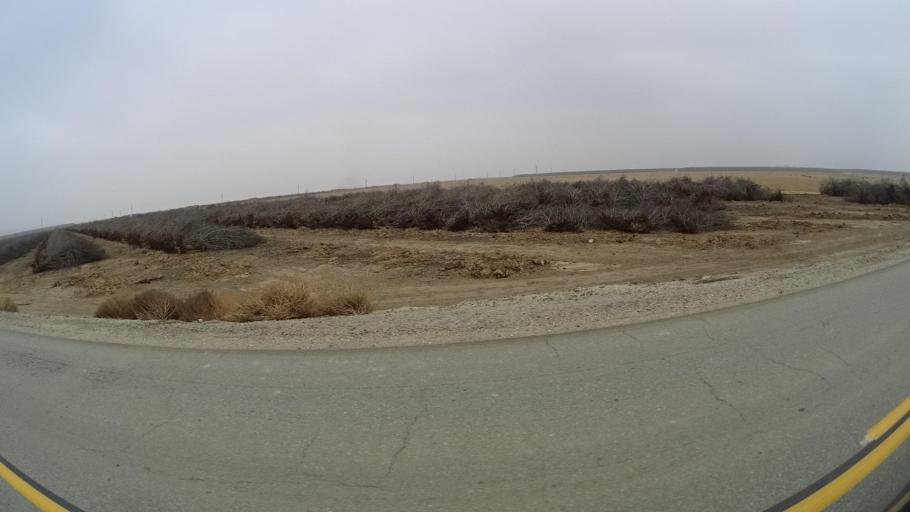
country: US
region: California
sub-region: Kern County
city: Maricopa
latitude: 35.1039
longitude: -119.3418
